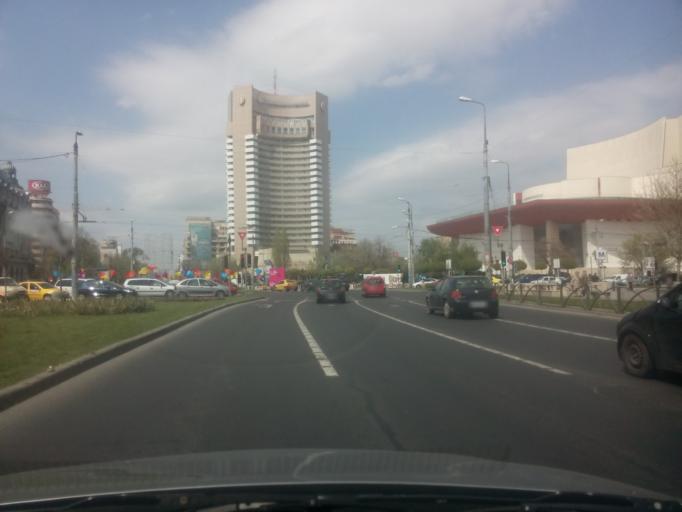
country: RO
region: Bucuresti
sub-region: Municipiul Bucuresti
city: Bucharest
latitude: 44.4350
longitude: 26.1028
